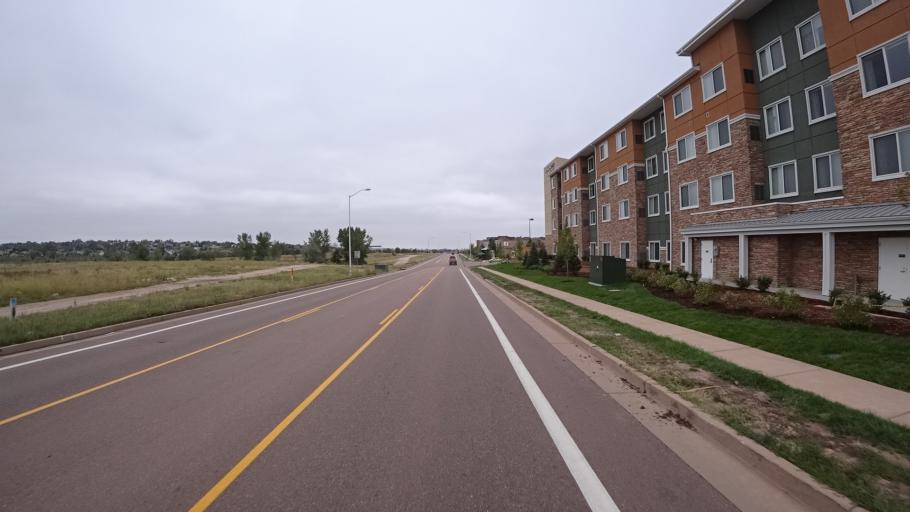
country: US
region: Colorado
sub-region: El Paso County
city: Cimarron Hills
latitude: 38.8783
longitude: -104.7152
